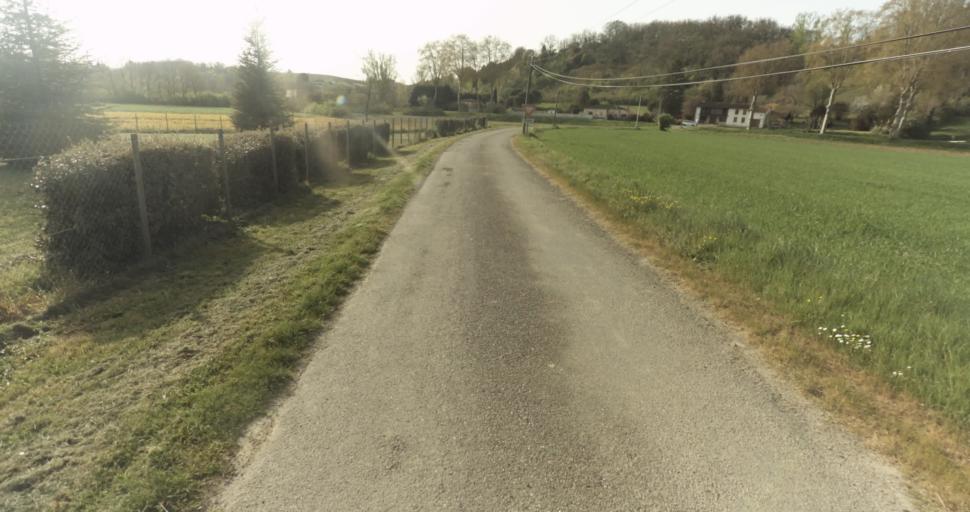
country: FR
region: Midi-Pyrenees
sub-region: Departement du Tarn-et-Garonne
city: Moissac
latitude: 44.1200
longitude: 1.1277
